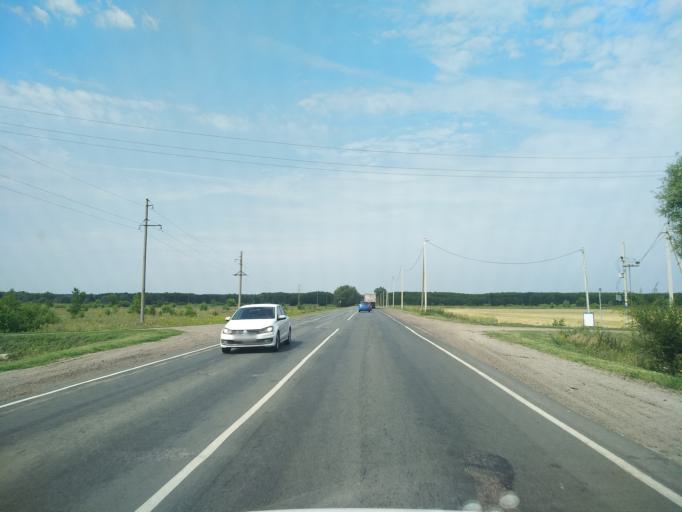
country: RU
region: Voronezj
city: Orlovo
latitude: 51.6804
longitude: 39.6093
